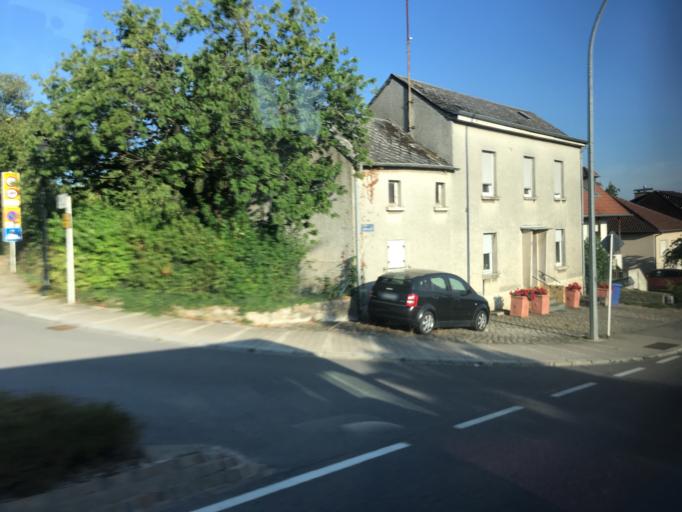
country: LU
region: Luxembourg
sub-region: Canton d'Esch-sur-Alzette
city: Frisange
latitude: 49.5235
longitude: 6.1848
